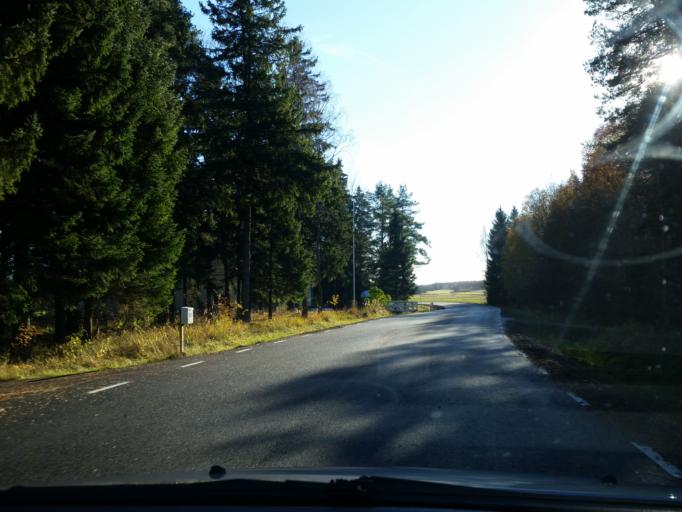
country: AX
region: Alands landsbygd
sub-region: Jomala
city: Jomala
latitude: 60.1990
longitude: 19.9579
